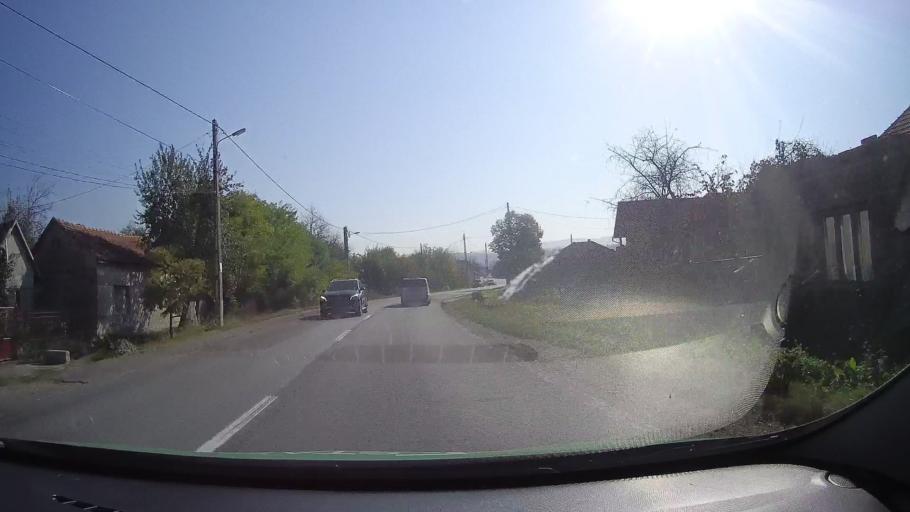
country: RO
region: Hunedoara
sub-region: Comuna Dobra
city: Dobra
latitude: 45.9175
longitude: 22.5601
